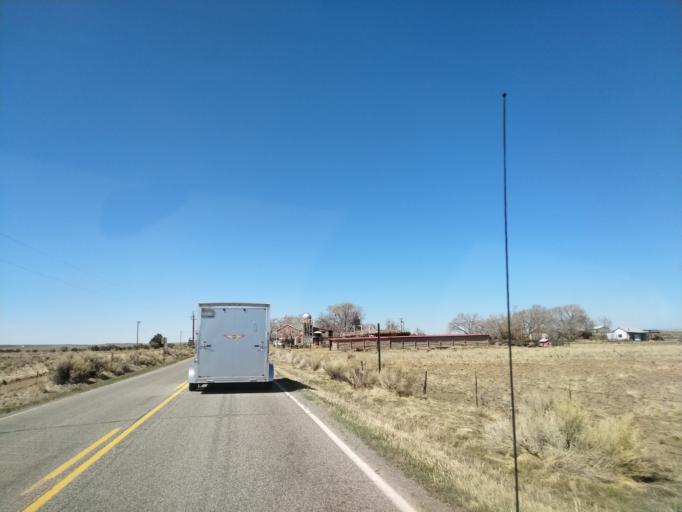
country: US
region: Colorado
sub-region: Mesa County
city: Redlands
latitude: 38.9938
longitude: -108.7383
